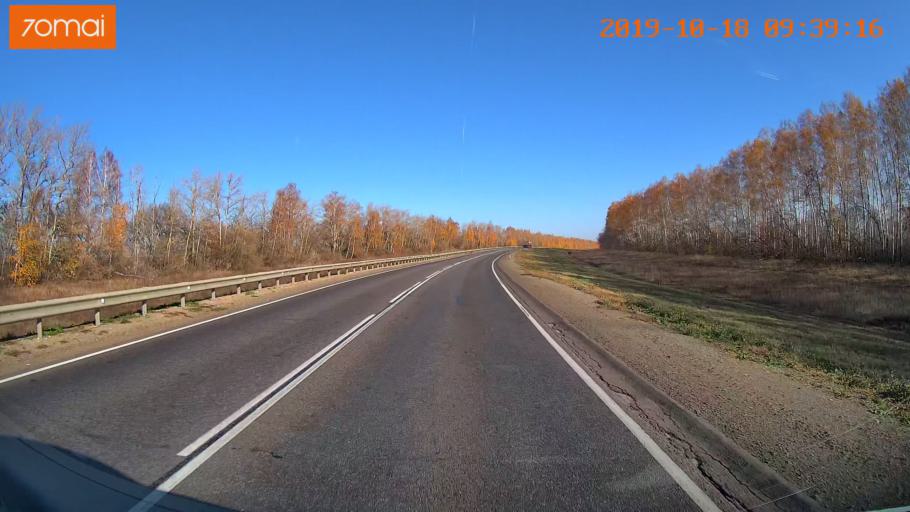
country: RU
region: Tula
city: Yefremov
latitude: 53.2507
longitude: 38.1344
